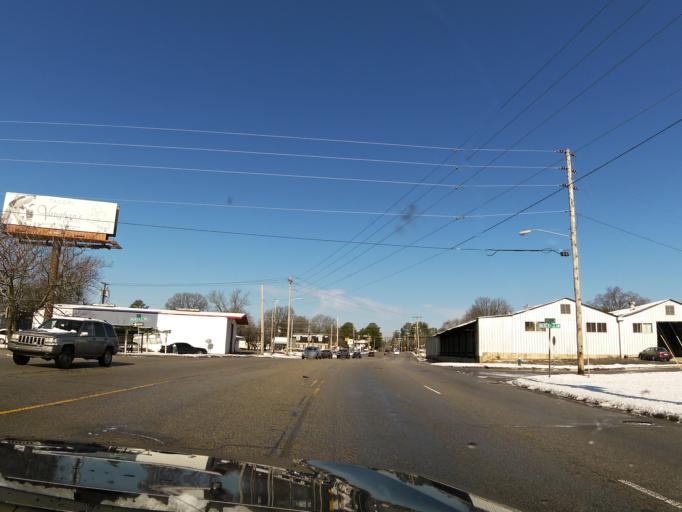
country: US
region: North Carolina
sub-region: Wilson County
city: Wilson
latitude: 35.7220
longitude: -77.9164
